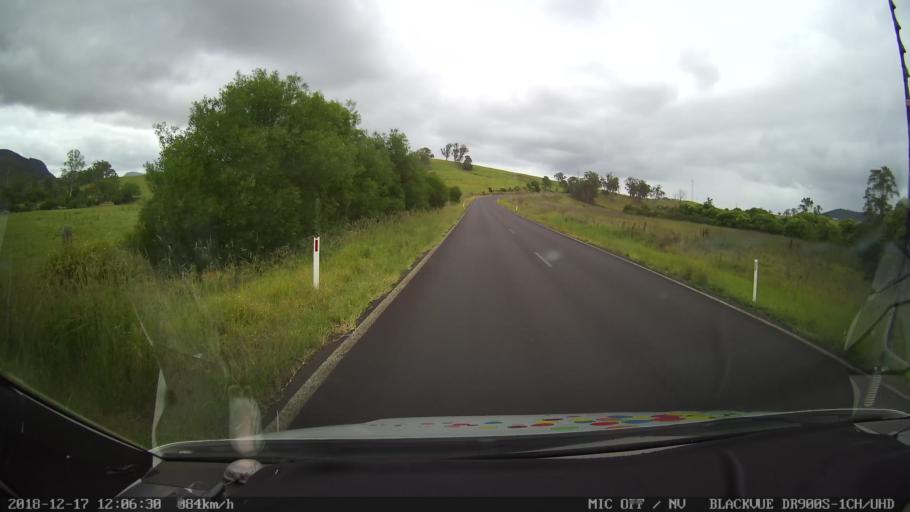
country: AU
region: New South Wales
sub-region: Kyogle
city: Kyogle
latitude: -28.4817
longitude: 152.5664
